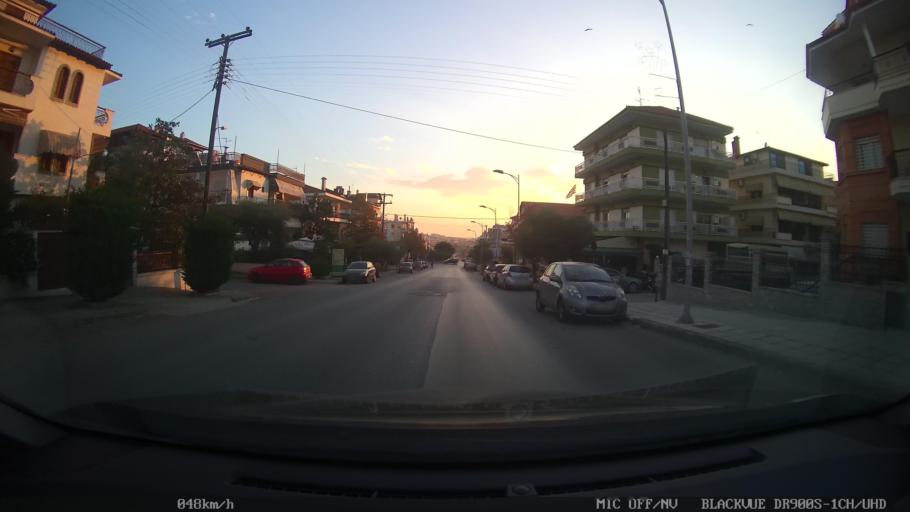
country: GR
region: Central Macedonia
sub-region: Nomos Thessalonikis
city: Pylaia
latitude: 40.6100
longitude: 22.9918
